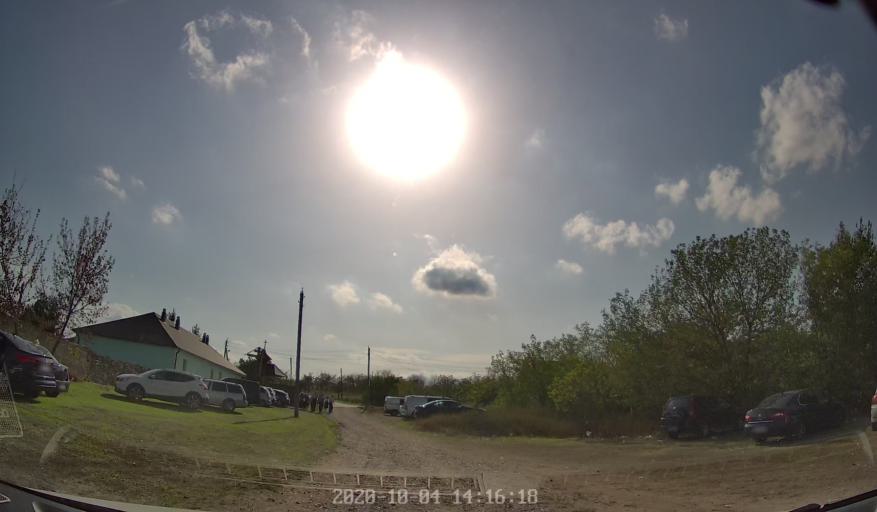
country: MD
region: Rezina
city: Saharna
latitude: 47.6038
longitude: 28.9847
